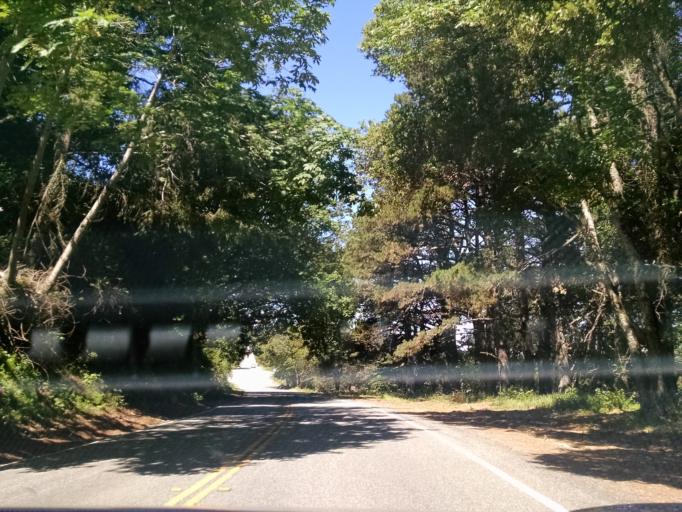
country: US
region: California
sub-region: San Mateo County
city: Portola Valley
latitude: 37.3405
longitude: -122.2182
